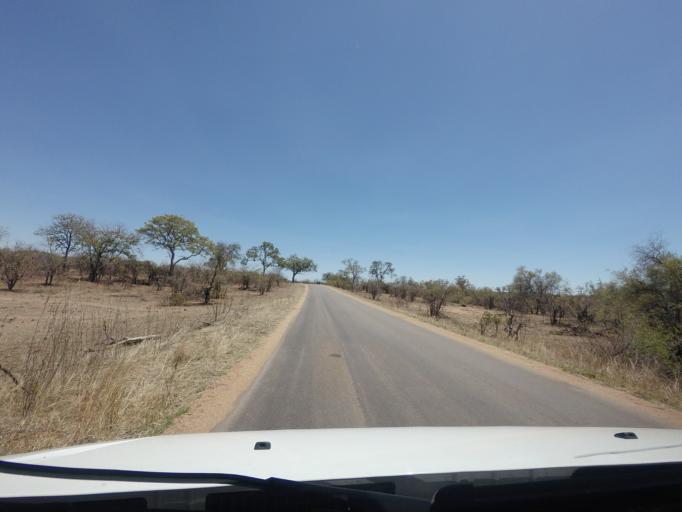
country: ZA
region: Limpopo
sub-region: Mopani District Municipality
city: Phalaborwa
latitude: -23.5557
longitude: 31.4471
